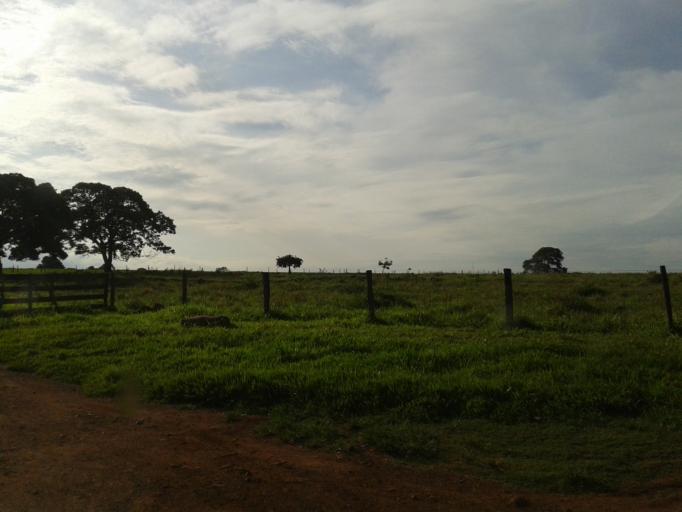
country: BR
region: Minas Gerais
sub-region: Centralina
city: Centralina
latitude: -18.7120
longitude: -49.1962
